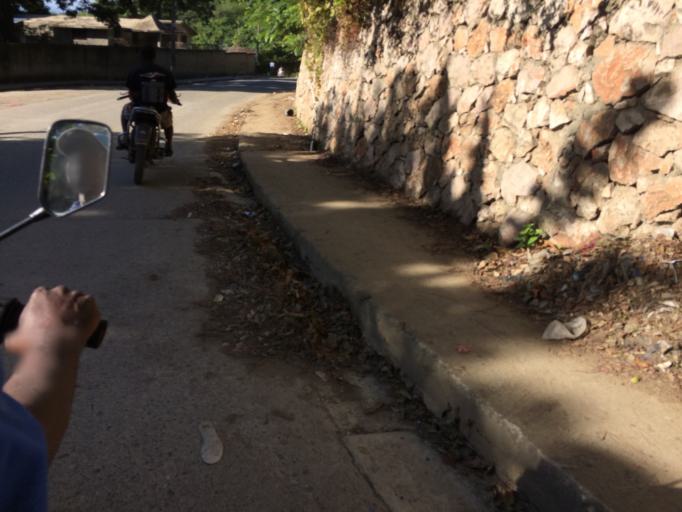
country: HT
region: Nord
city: Okap
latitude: 19.7502
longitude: -72.2150
